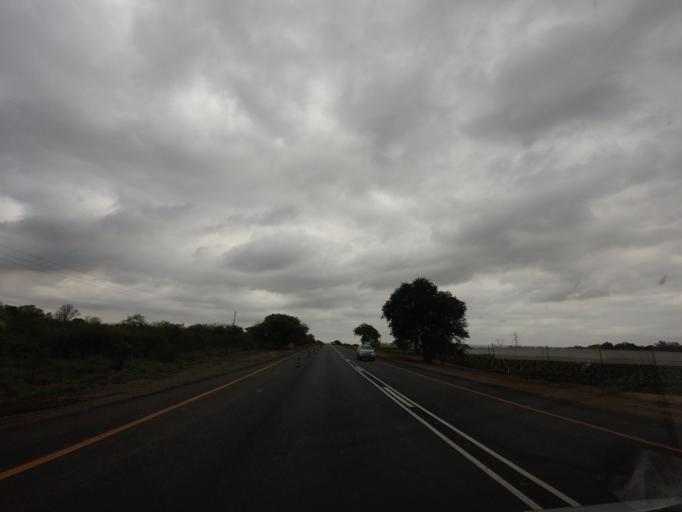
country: ZA
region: Mpumalanga
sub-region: Ehlanzeni District
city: Komatipoort
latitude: -25.4373
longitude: 31.7982
